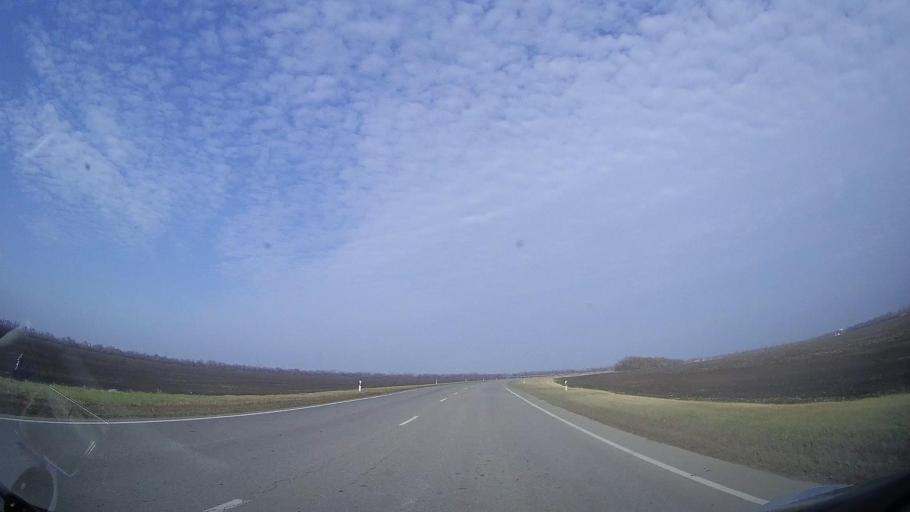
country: RU
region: Rostov
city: Tselina
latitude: 46.5164
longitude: 40.9958
